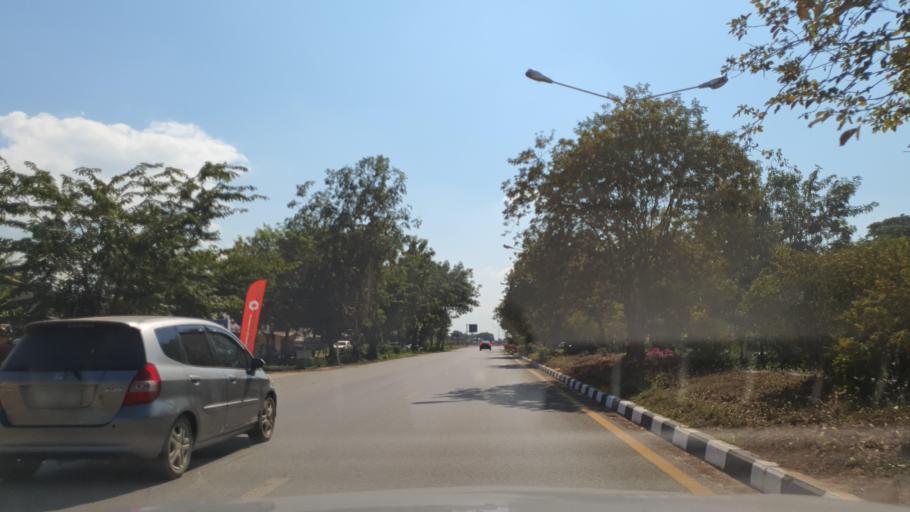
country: TH
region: Nan
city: Nan
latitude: 18.8033
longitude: 100.7780
